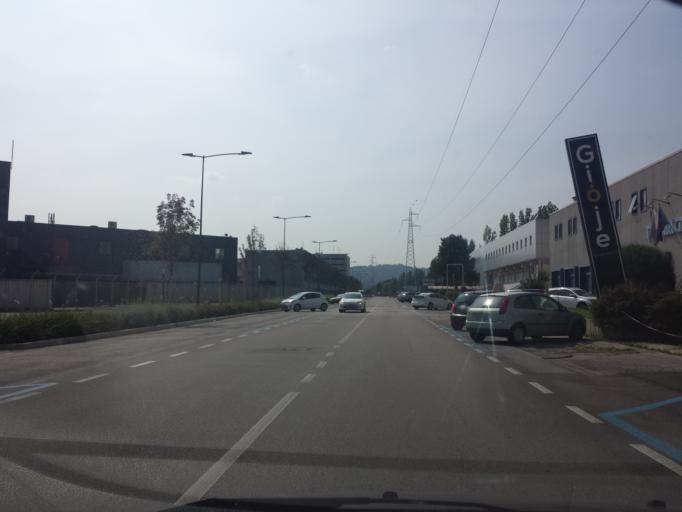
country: IT
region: Veneto
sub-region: Provincia di Vicenza
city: Creazzo
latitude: 45.5302
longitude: 11.5061
